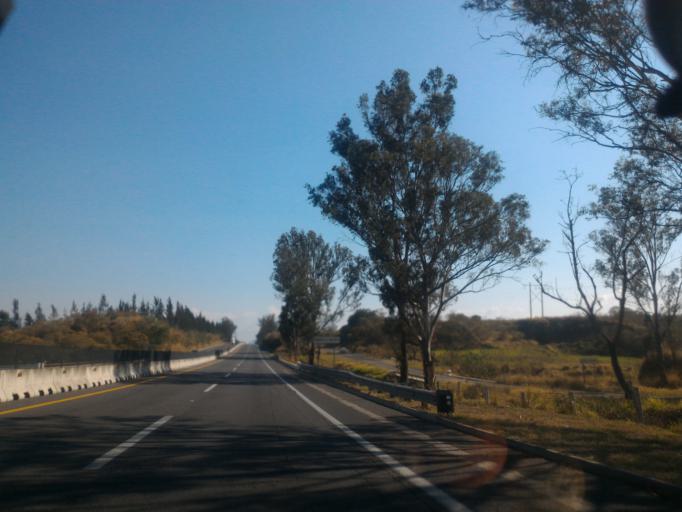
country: MX
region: Jalisco
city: Zapotiltic
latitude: 19.6238
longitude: -103.4634
